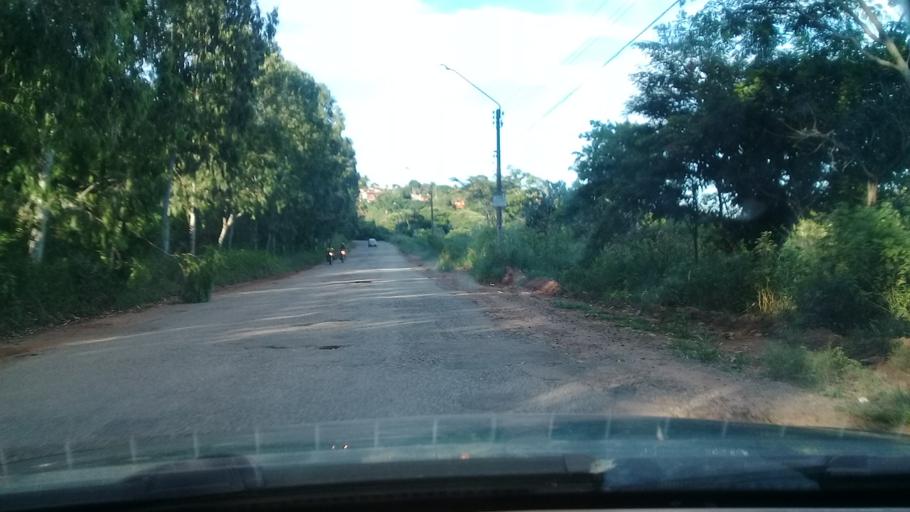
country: BR
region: Pernambuco
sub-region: Vicencia
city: Vicencia
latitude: -7.6150
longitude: -35.2374
